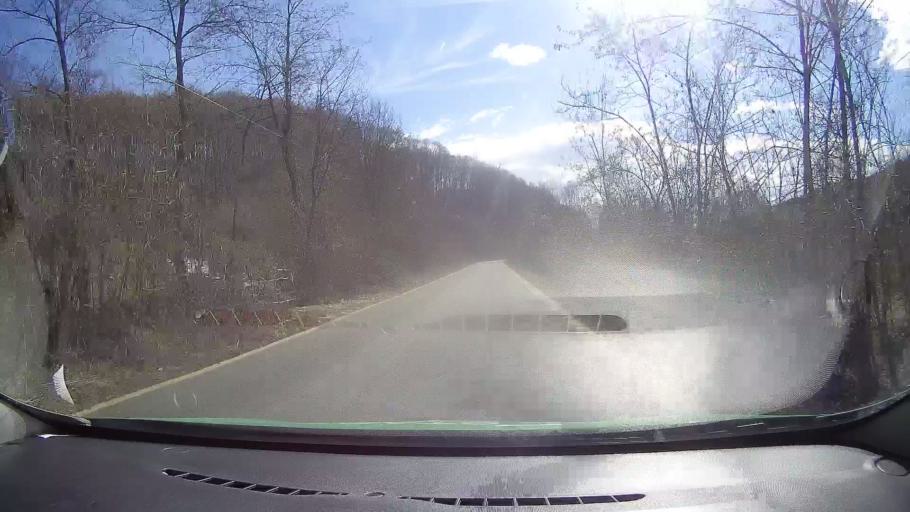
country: RO
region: Dambovita
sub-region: Comuna Vulcana-Pandele
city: Gura Vulcanei
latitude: 45.0469
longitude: 25.3883
